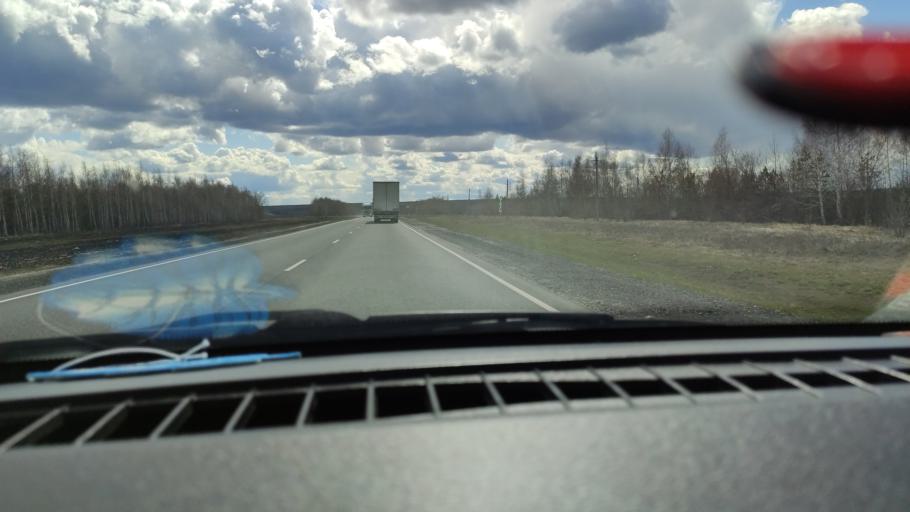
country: RU
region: Samara
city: Syzran'
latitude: 52.9849
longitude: 48.3164
